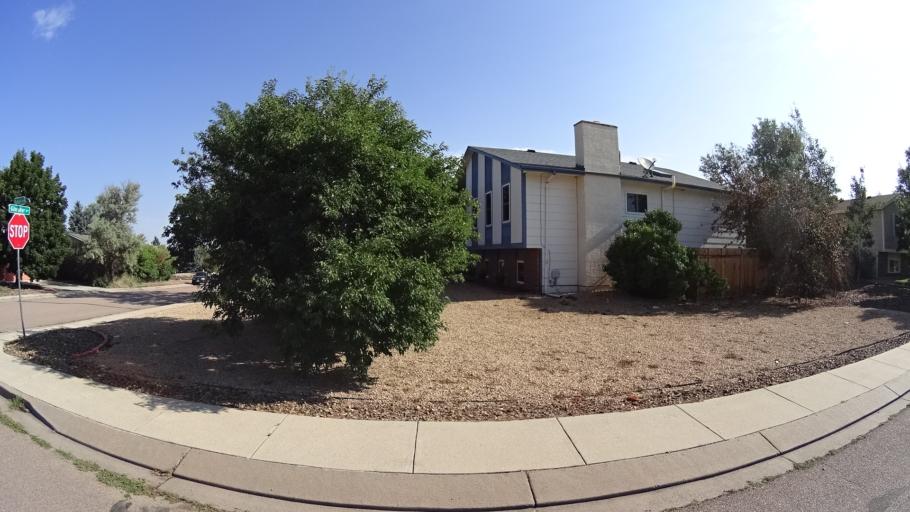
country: US
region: Colorado
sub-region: El Paso County
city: Black Forest
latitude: 38.9432
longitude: -104.7720
